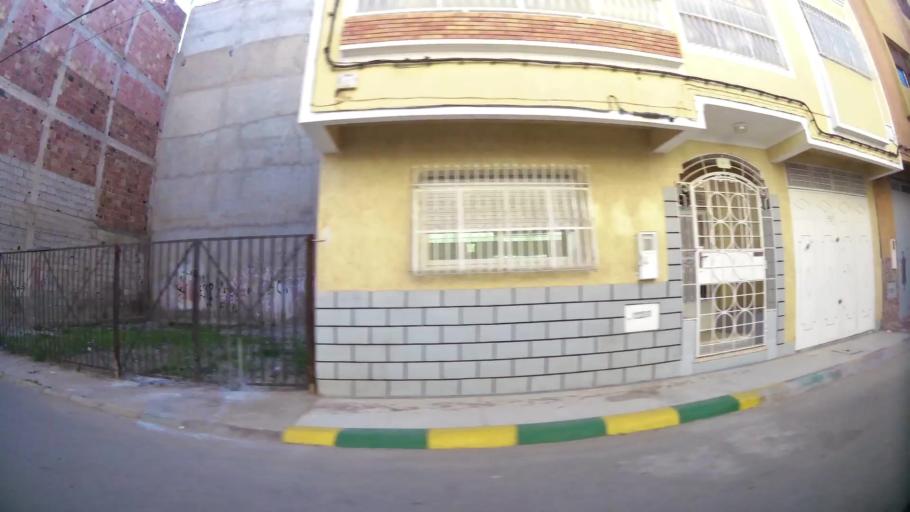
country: MA
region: Oriental
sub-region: Berkane-Taourirt
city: Berkane
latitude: 34.9333
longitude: -2.3288
